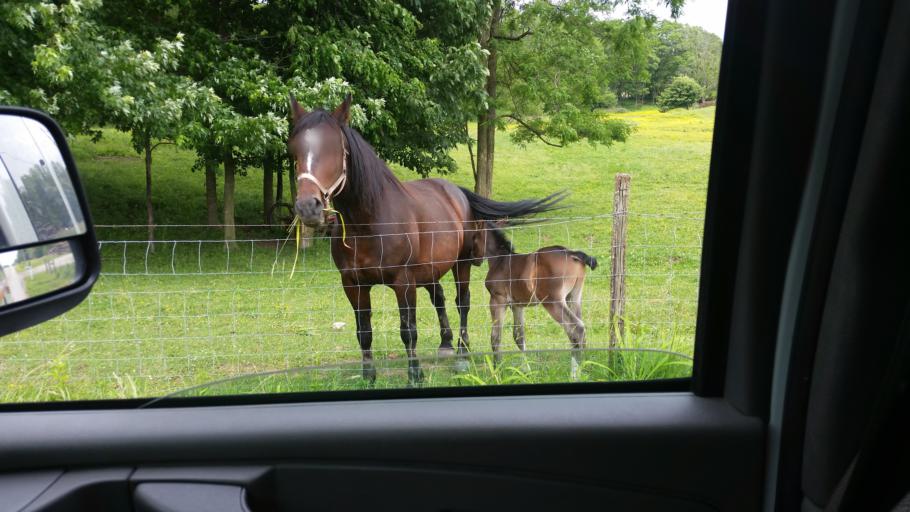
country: US
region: Ohio
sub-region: Richland County
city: Lexington
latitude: 40.5839
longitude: -82.6431
